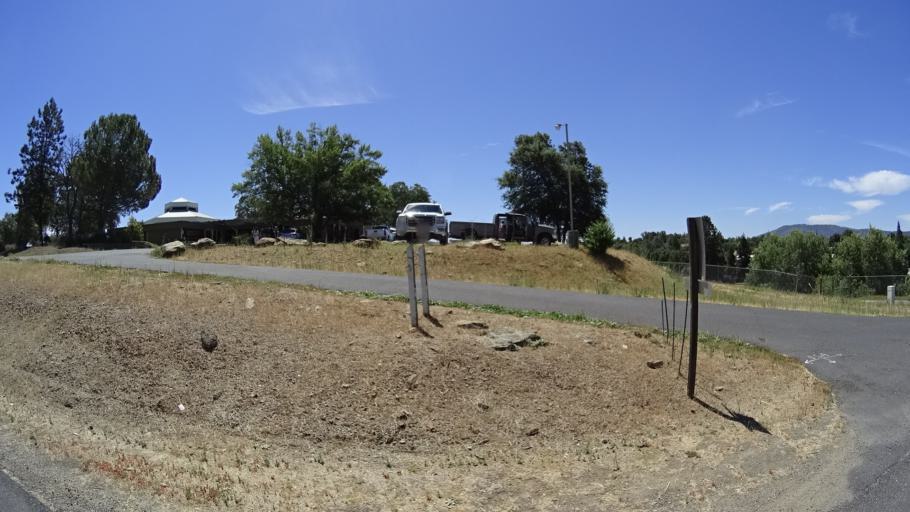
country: US
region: California
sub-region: Calaveras County
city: Angels Camp
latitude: 38.0818
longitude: -120.5483
